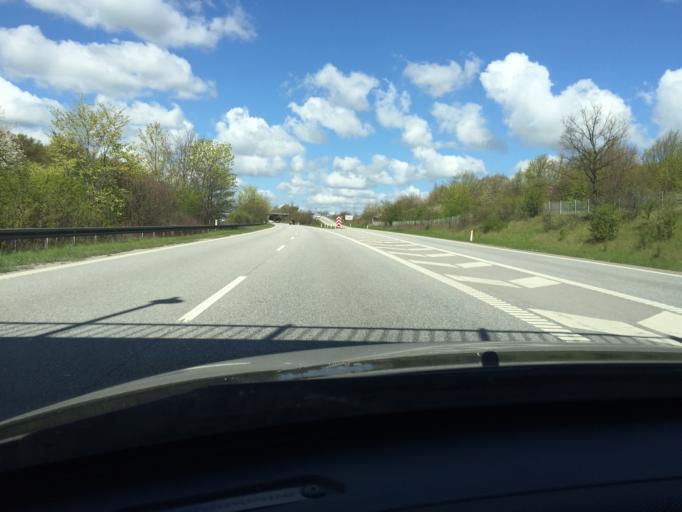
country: DK
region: Capital Region
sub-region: Fureso Kommune
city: Stavnsholt
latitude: 55.8209
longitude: 12.3826
